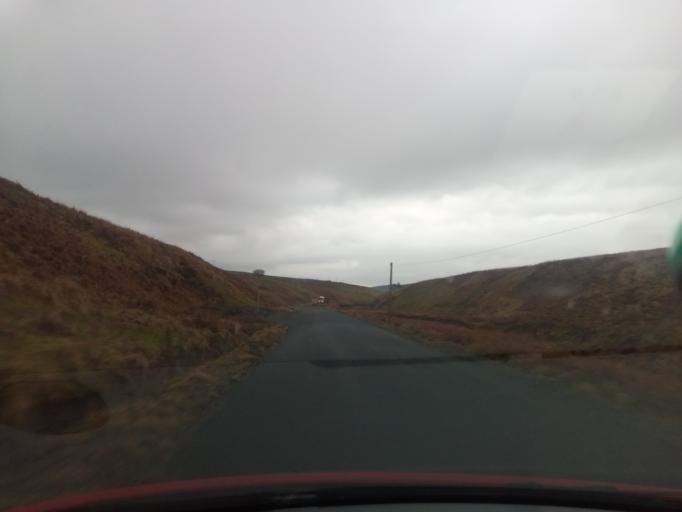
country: GB
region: Scotland
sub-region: The Scottish Borders
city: Hawick
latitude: 55.2775
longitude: -2.6790
